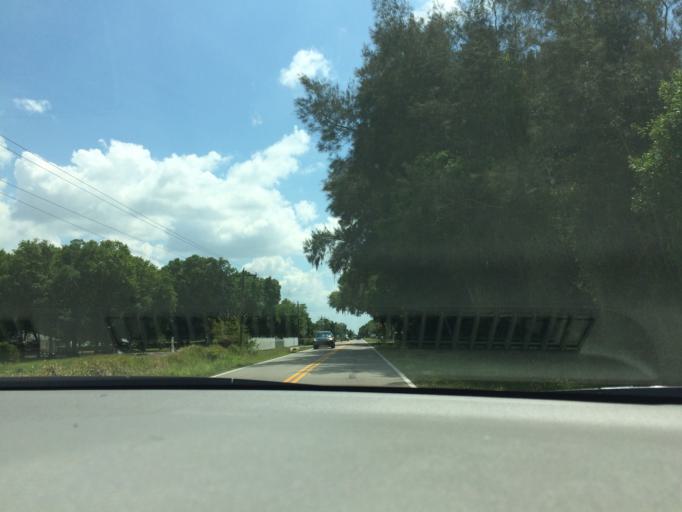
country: US
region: Florida
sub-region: Sarasota County
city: The Meadows
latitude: 27.4546
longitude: -82.3955
